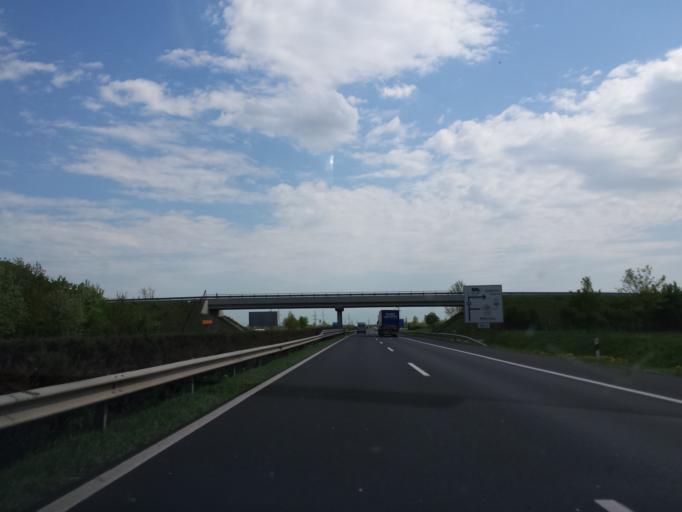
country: HU
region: Gyor-Moson-Sopron
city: Mosonmagyarovar
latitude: 47.8588
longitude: 17.2387
